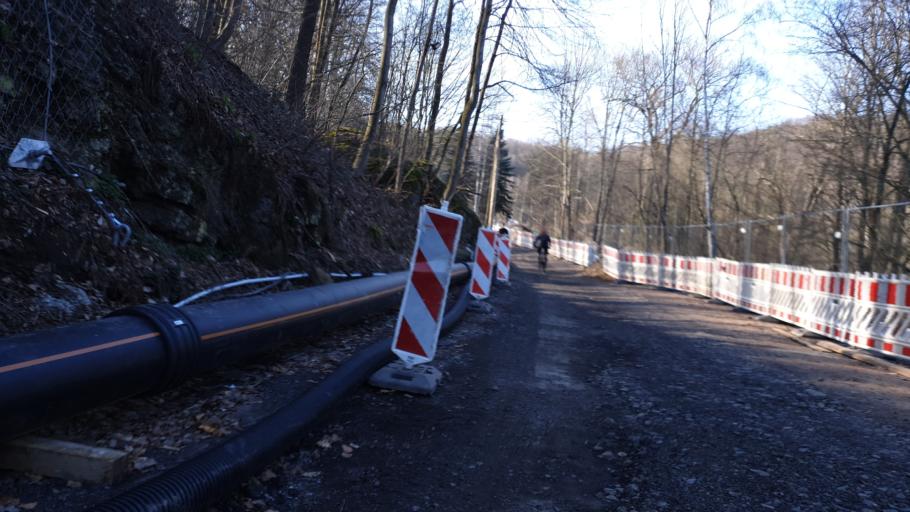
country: DE
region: Saxony
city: Taura
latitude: 50.9344
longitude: 12.8514
